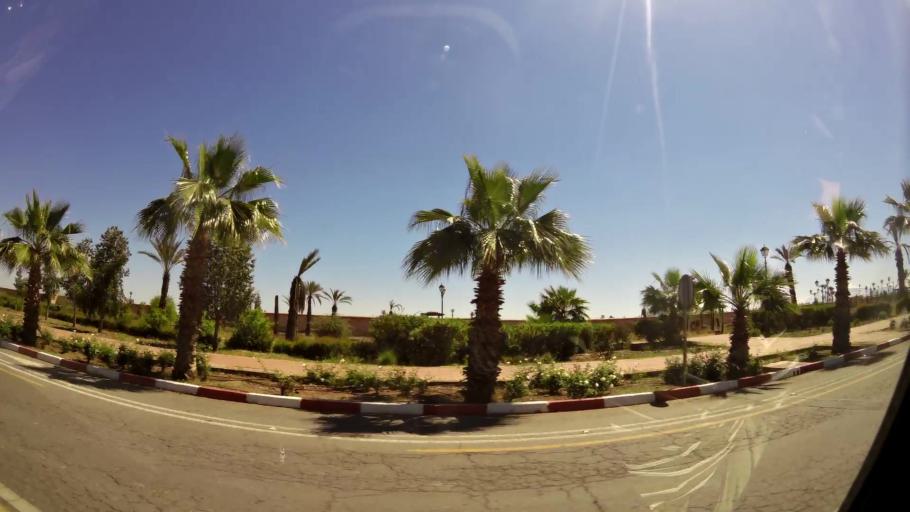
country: MA
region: Marrakech-Tensift-Al Haouz
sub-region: Marrakech
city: Marrakesh
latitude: 31.5886
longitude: -7.9846
